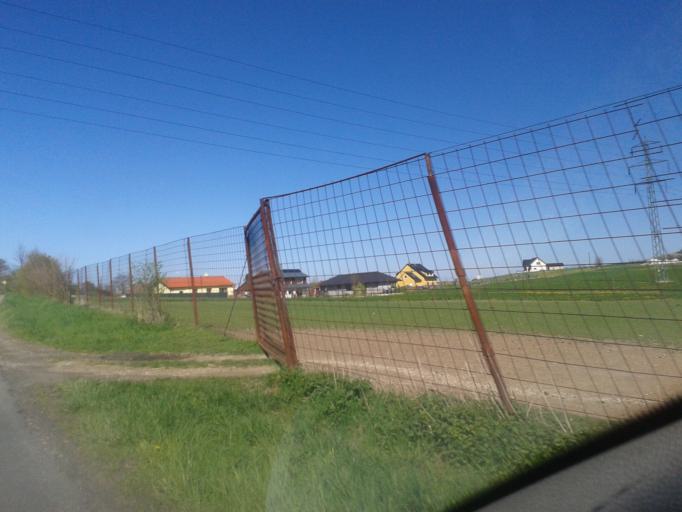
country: CZ
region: Central Bohemia
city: Revnice
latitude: 49.8970
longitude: 14.1413
